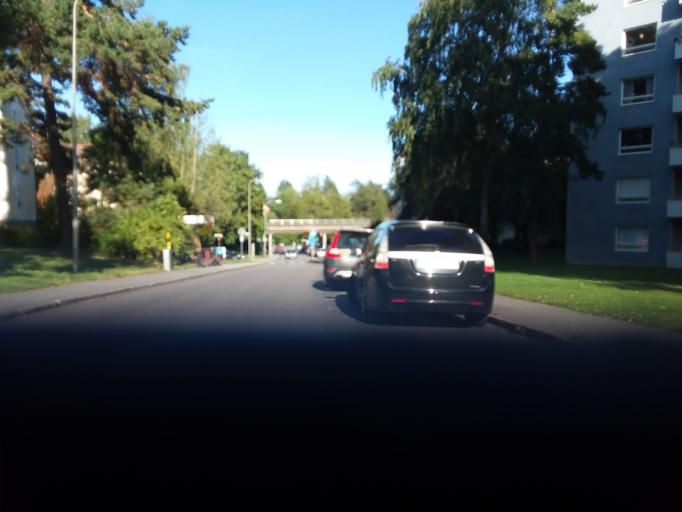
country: SE
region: Stockholm
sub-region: Stockholms Kommun
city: Bromma
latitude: 59.3490
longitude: 17.8796
